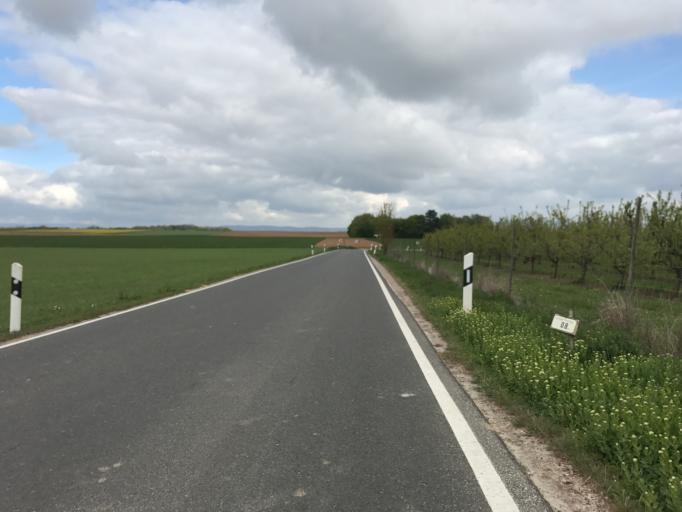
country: DE
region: Rheinland-Pfalz
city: Engelstadt
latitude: 49.8980
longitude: 8.0579
